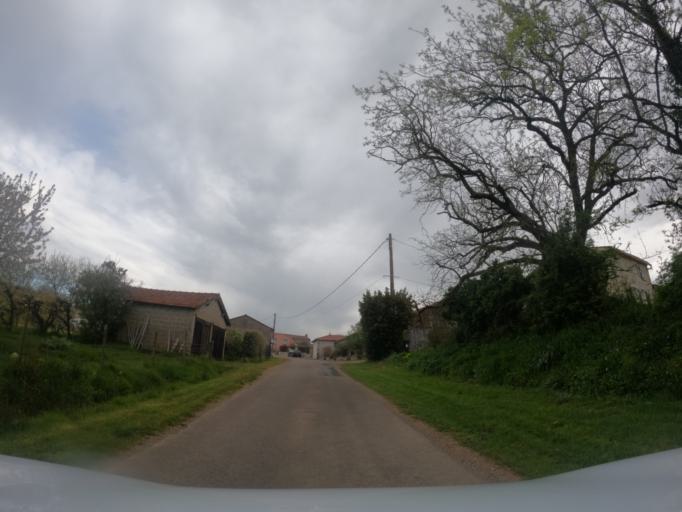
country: FR
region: Pays de la Loire
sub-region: Departement de la Vendee
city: Le Champ-Saint-Pere
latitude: 46.5201
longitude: -1.3261
